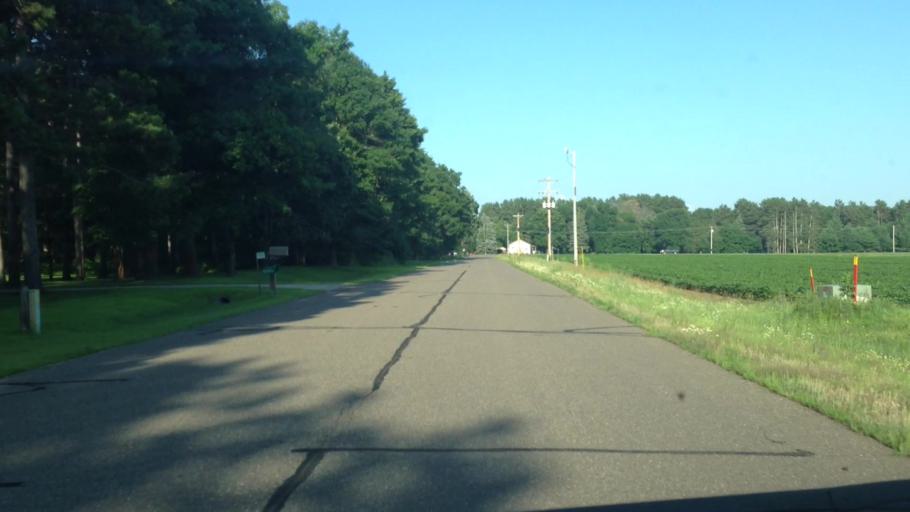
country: US
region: Minnesota
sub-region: Sherburne County
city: Big Lake
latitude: 45.4440
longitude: -93.7402
